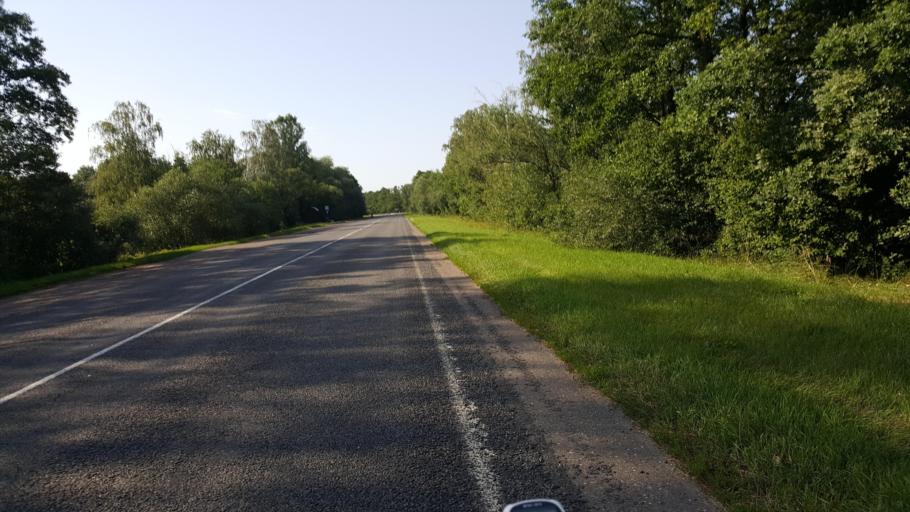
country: BY
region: Brest
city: Zhabinka
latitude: 52.2961
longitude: 23.9374
